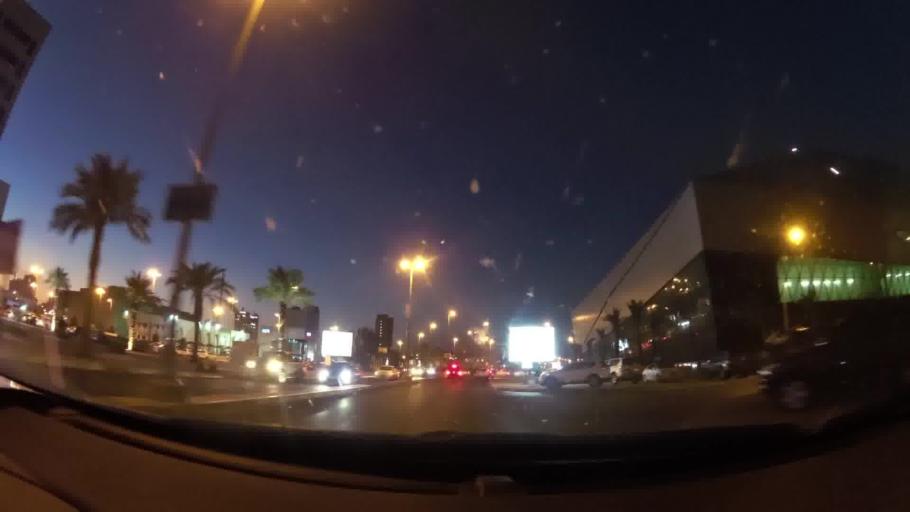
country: KW
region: Muhafazat Hawalli
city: As Salimiyah
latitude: 29.3393
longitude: 48.0847
